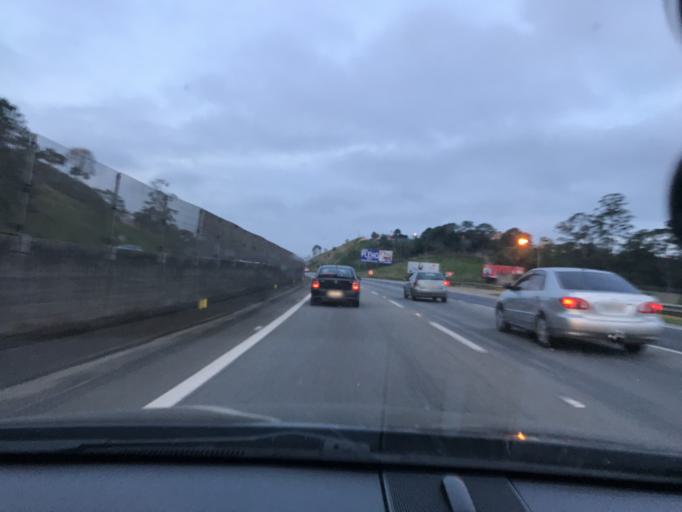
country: BR
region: Sao Paulo
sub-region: Itaquaquecetuba
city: Itaquaquecetuba
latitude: -23.4702
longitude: -46.3992
